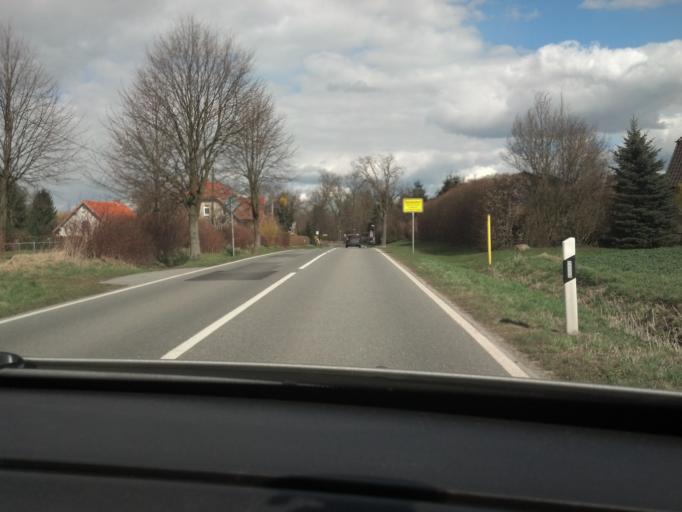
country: DE
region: Mecklenburg-Vorpommern
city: Loitz
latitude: 53.4548
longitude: 13.3563
